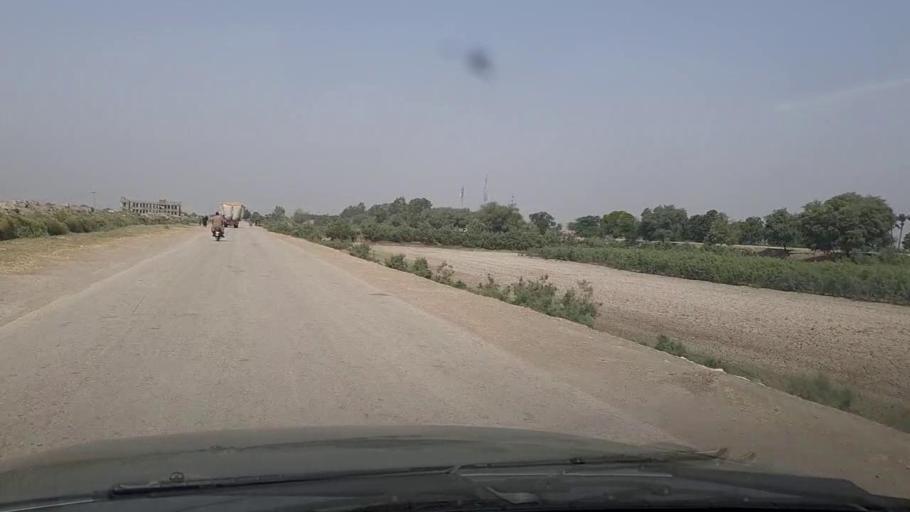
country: PK
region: Sindh
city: Thul
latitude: 28.3230
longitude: 68.7439
